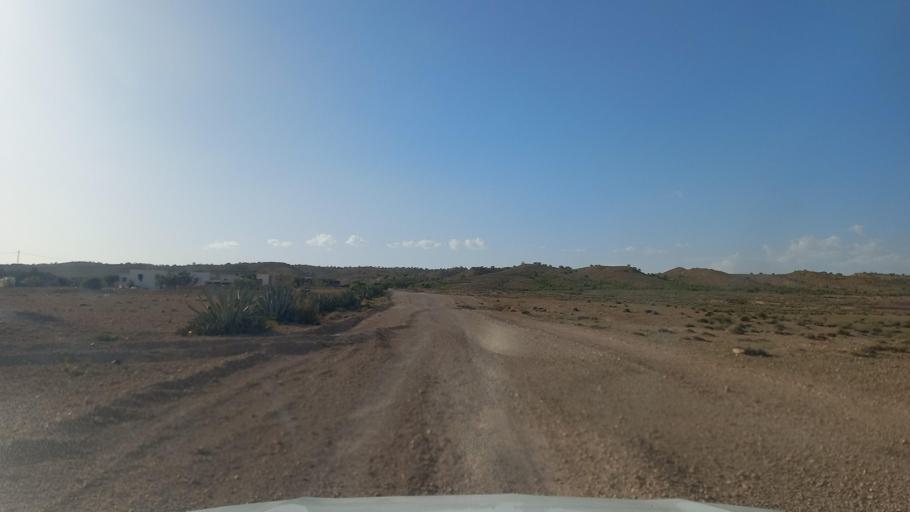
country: TN
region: Al Qasrayn
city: Sbiba
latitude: 35.3636
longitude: 9.0005
